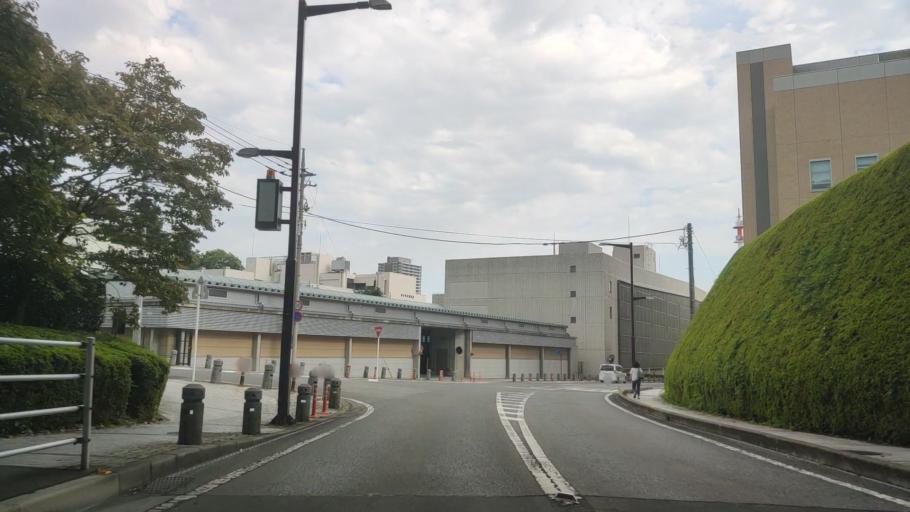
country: JP
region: Tochigi
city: Utsunomiya-shi
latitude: 36.5664
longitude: 139.8846
